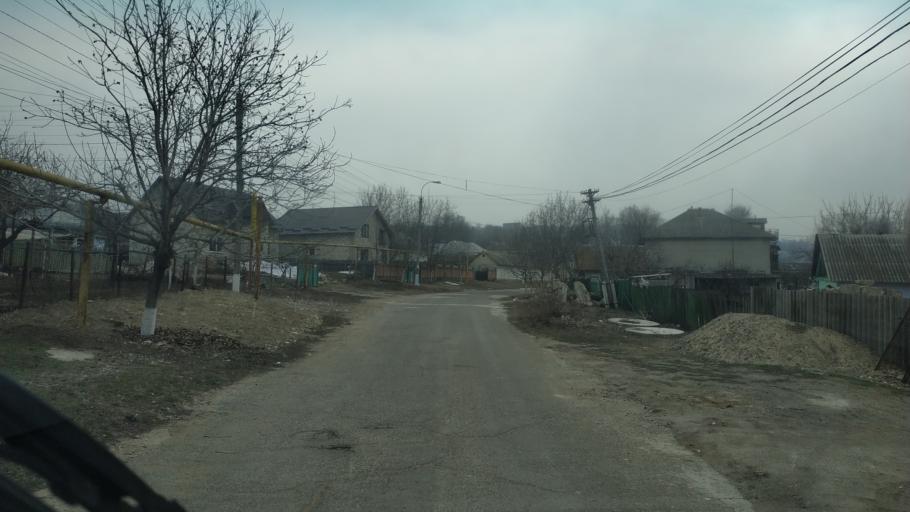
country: MD
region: Chisinau
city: Singera
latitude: 46.9191
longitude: 28.9822
